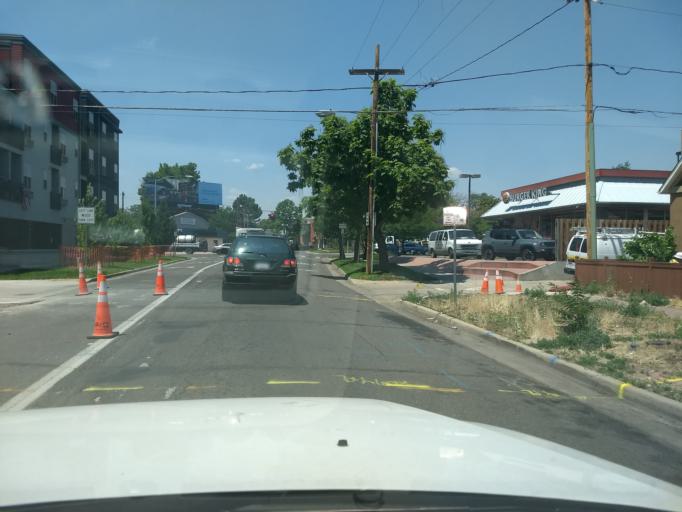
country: US
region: Colorado
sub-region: Denver County
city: Denver
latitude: 39.7620
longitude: -104.9725
